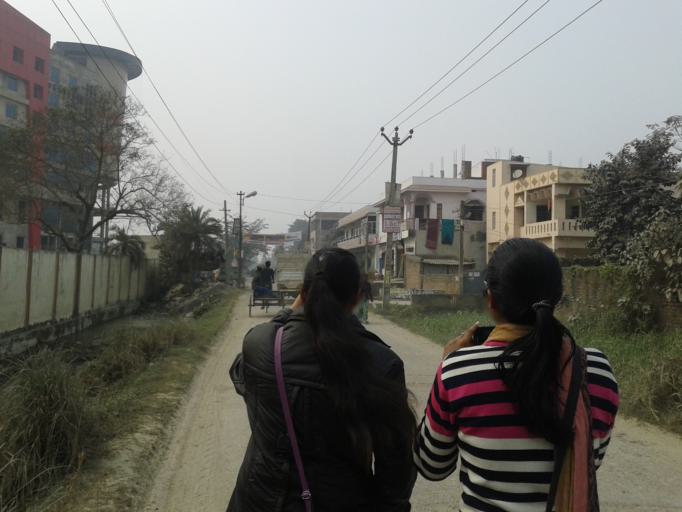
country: IN
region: Bihar
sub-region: Muzaffarpur
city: Muzaffarpur
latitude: 26.1020
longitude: 85.4102
